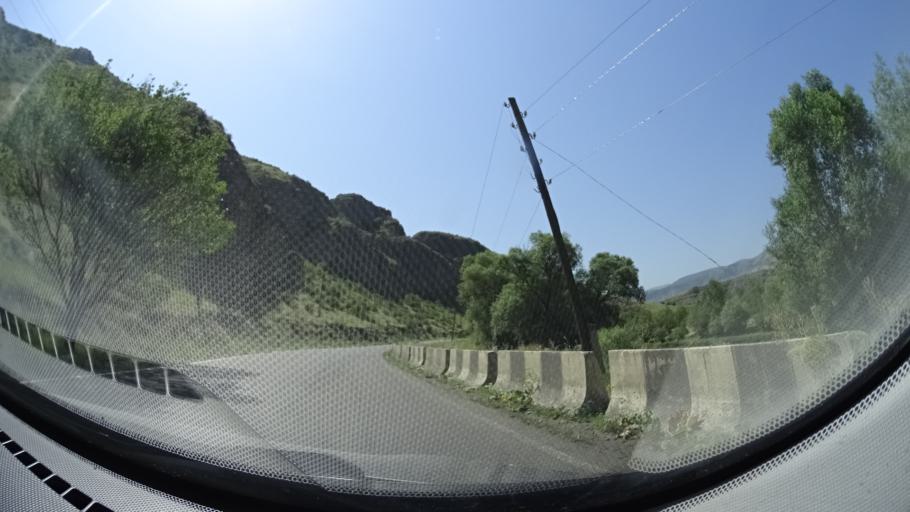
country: GE
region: Samtskhe-Javakheti
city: Aspindza
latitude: 41.5437
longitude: 43.2618
